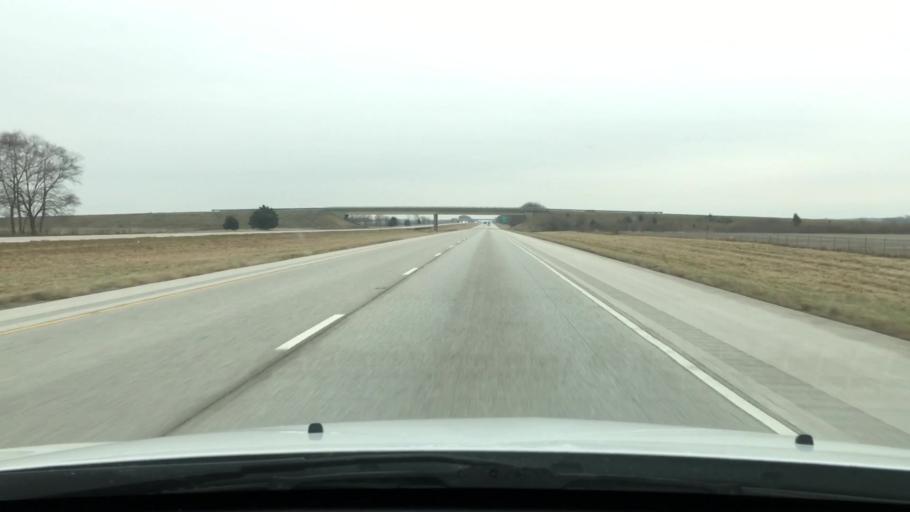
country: US
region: Illinois
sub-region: Scott County
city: Winchester
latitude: 39.6801
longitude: -90.3505
